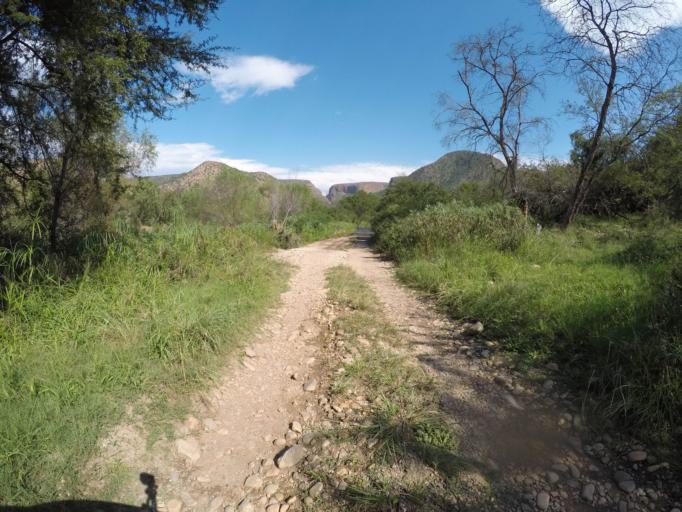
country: ZA
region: Eastern Cape
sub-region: Cacadu District Municipality
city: Kareedouw
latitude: -33.6656
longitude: 24.3865
